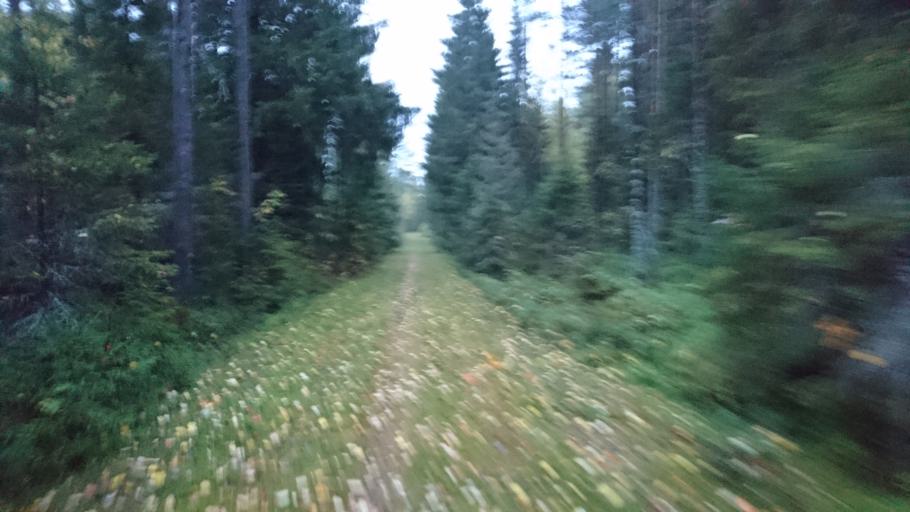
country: SE
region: Vaesterbotten
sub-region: Robertsfors Kommun
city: Robertsfors
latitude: 64.2299
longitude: 20.9965
